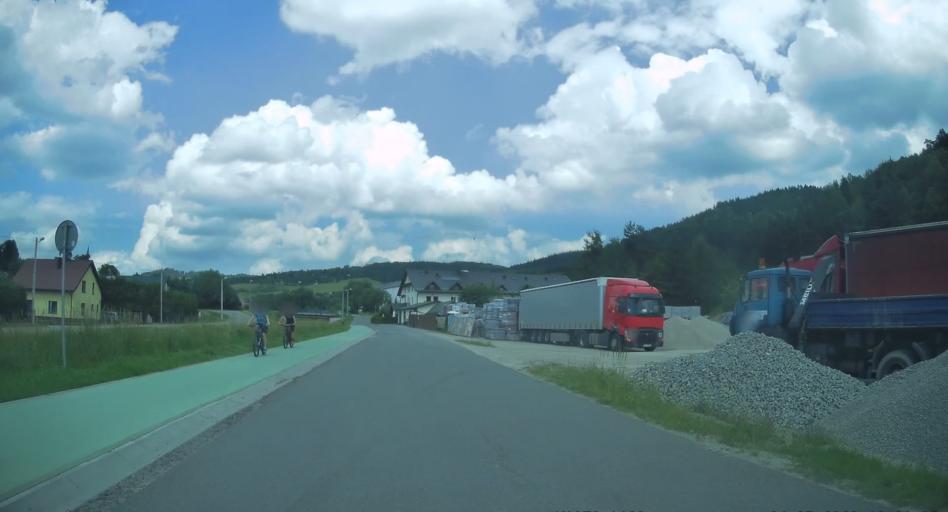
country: PL
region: Lesser Poland Voivodeship
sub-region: Powiat nowosadecki
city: Krynica-Zdroj
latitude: 49.3909
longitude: 20.9563
